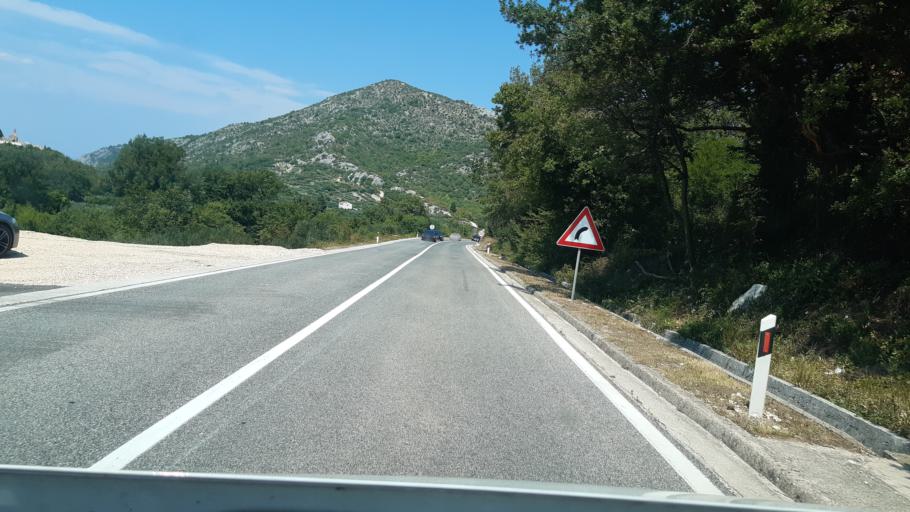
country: HR
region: Dubrovacko-Neretvanska
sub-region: Grad Dubrovnik
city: Opuzen
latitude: 42.9677
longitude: 17.5171
